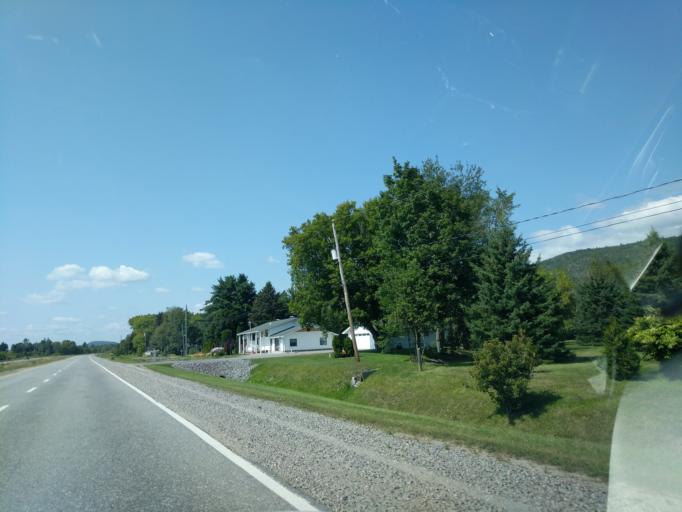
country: CA
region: Quebec
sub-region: Outaouais
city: Wakefield
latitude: 45.5252
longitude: -75.9952
